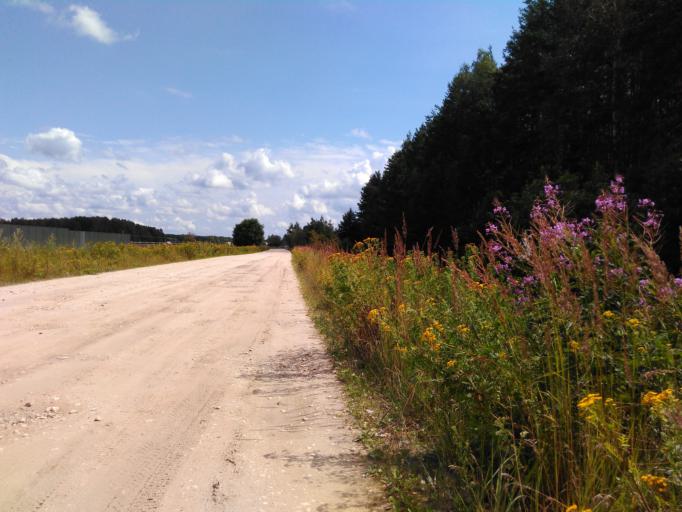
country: RU
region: Vladimir
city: Krasnyy Oktyabr'
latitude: 56.0030
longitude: 38.8433
